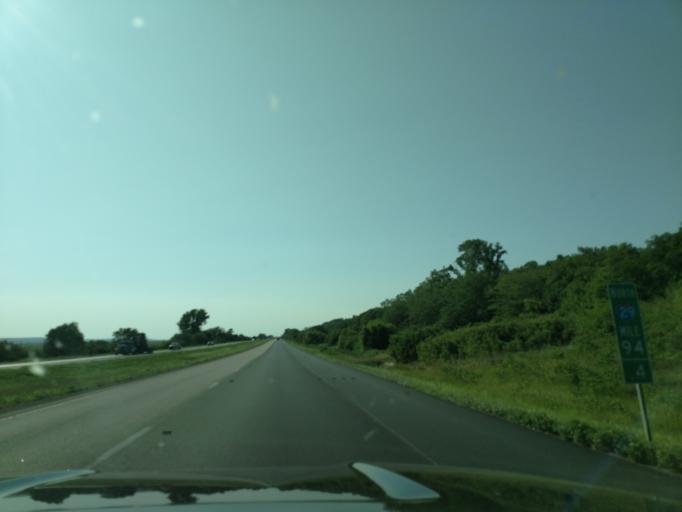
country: US
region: Missouri
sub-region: Holt County
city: Mound City
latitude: 40.2168
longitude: -95.3861
